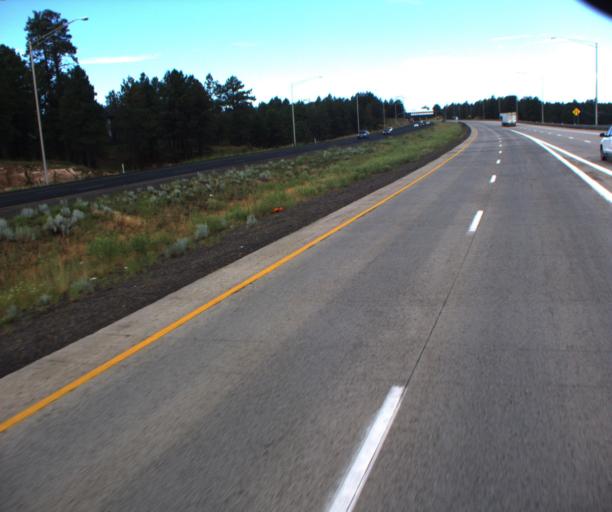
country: US
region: Arizona
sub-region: Coconino County
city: Flagstaff
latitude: 35.1666
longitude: -111.6700
